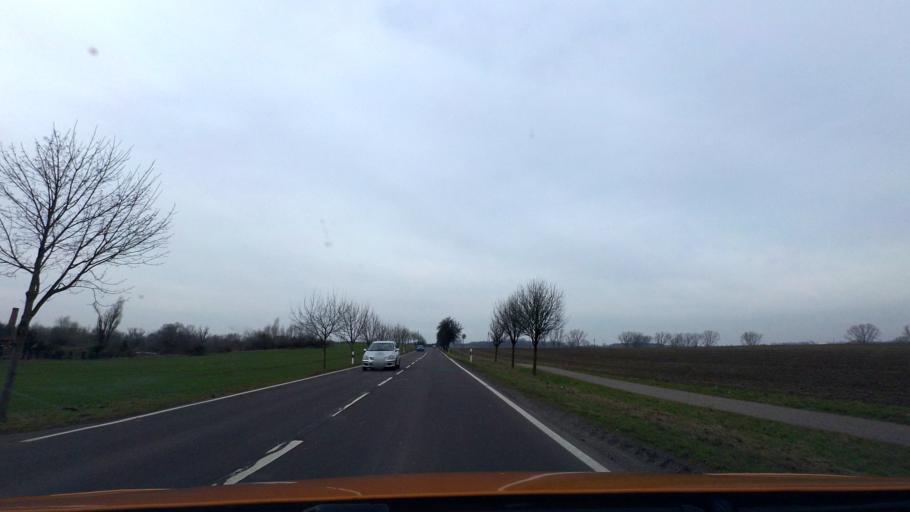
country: DE
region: Saxony-Anhalt
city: Dahlenwarsleben
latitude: 52.1580
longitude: 11.5325
